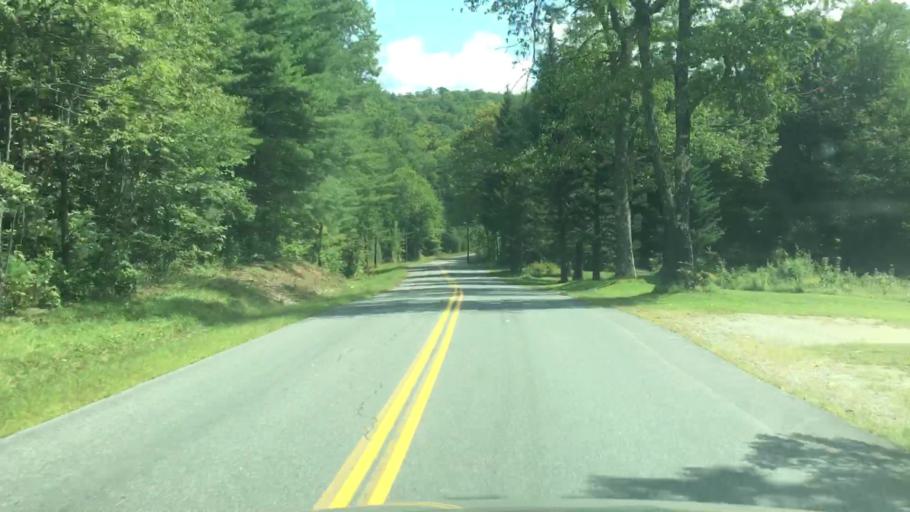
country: US
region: Vermont
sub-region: Windham County
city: Dover
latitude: 42.8157
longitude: -72.7418
